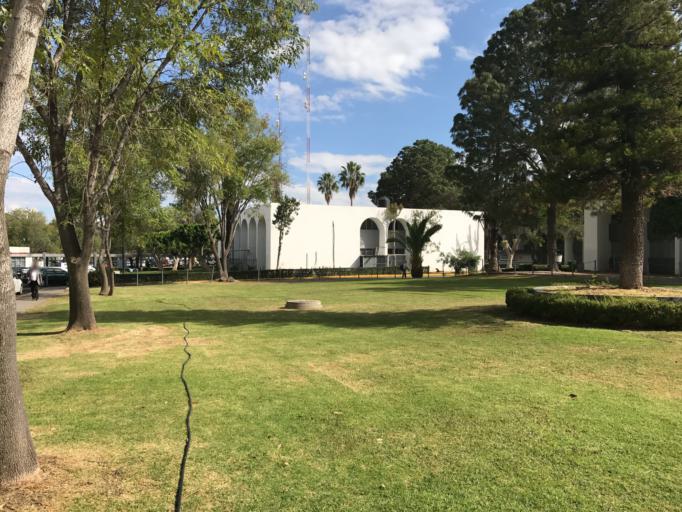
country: MX
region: Michoacan
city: Morelia
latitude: 19.6906
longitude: -101.2035
